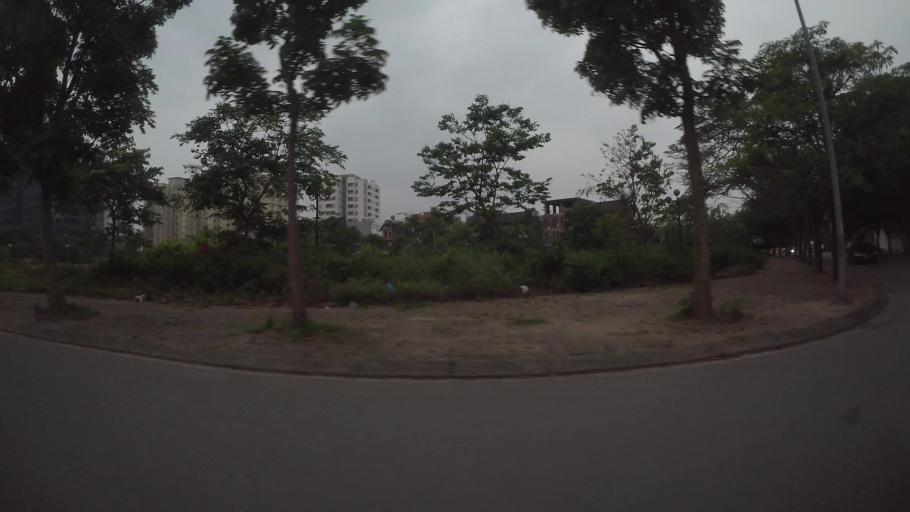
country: VN
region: Ha Noi
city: Trau Quy
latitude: 21.0401
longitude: 105.9109
